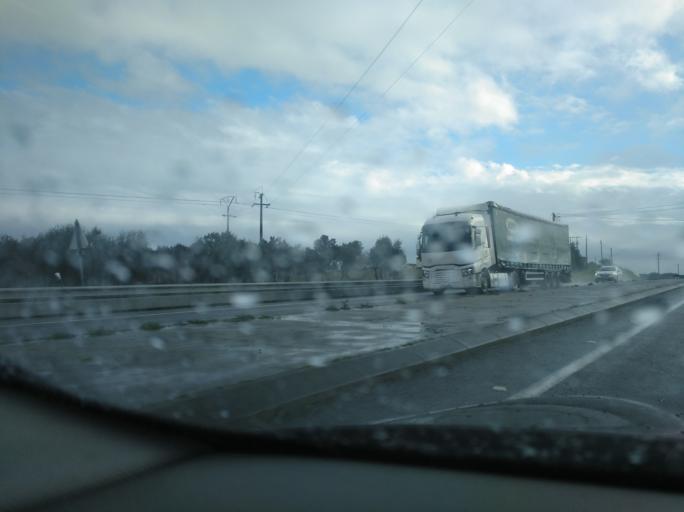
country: PT
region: Setubal
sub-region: Grandola
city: Grandola
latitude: 38.0744
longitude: -8.4165
